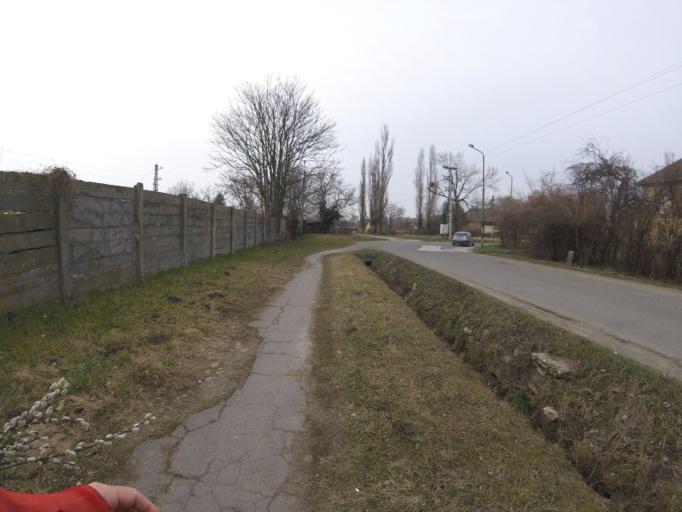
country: HU
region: Pest
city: Aszod
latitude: 47.6490
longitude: 19.4890
